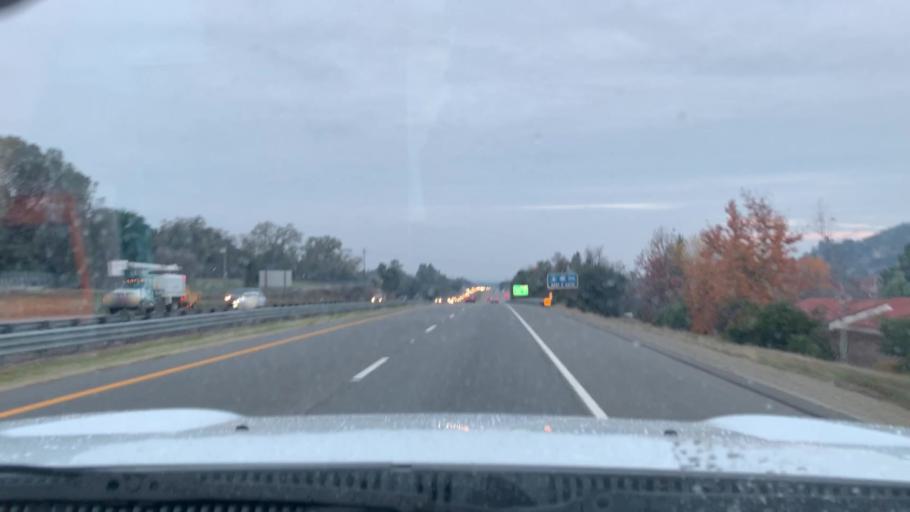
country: US
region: California
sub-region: San Luis Obispo County
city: Atascadero
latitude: 35.4573
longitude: -120.6444
